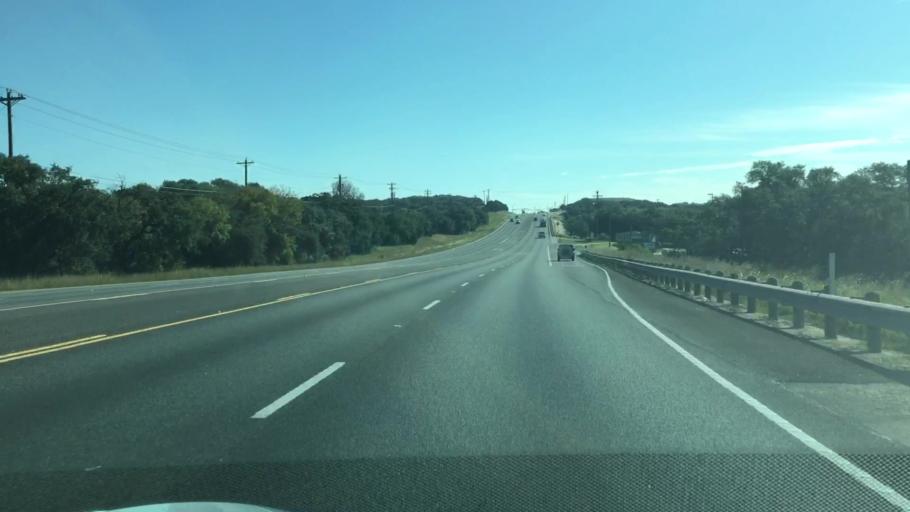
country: US
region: Texas
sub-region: Hays County
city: Dripping Springs
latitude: 30.1950
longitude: -98.0521
